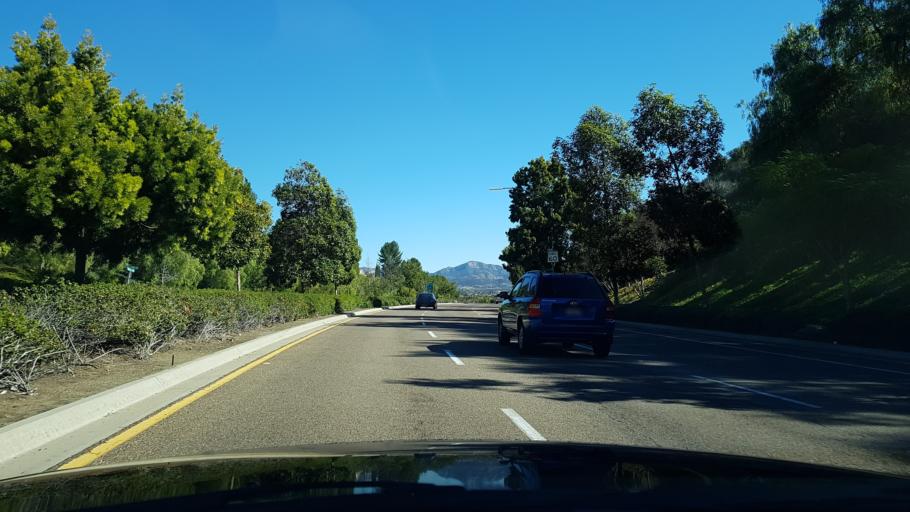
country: US
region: California
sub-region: San Diego County
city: Poway
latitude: 32.9713
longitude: -117.0783
